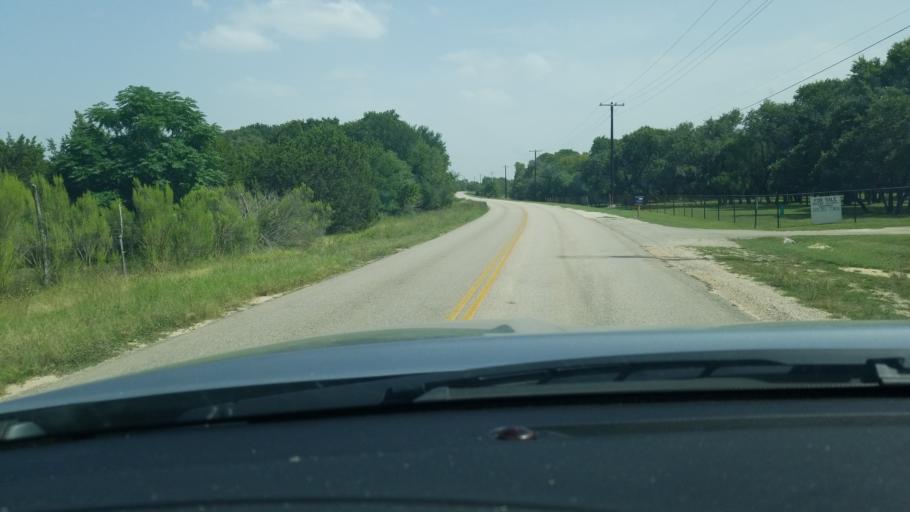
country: US
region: Texas
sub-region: Comal County
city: Bulverde
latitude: 29.7893
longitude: -98.4658
